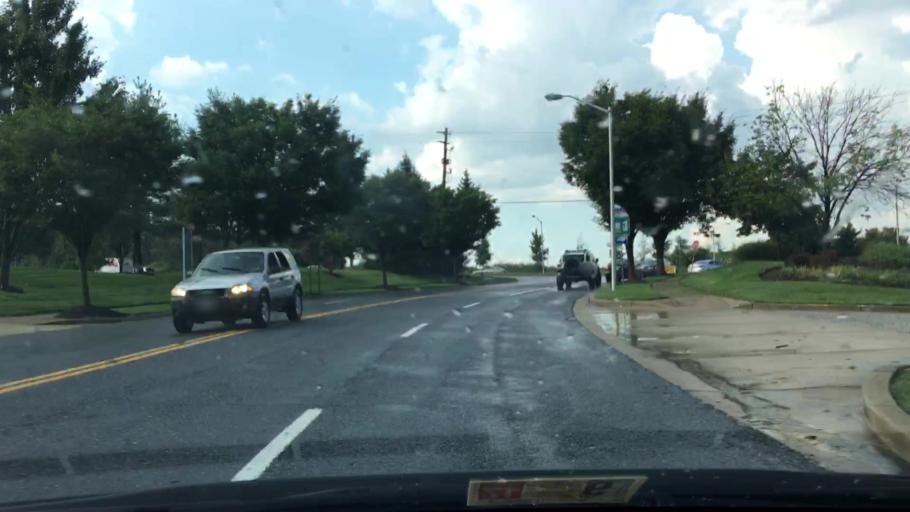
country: US
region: Maryland
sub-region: Prince George's County
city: Beltsville
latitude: 39.0627
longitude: -76.8892
